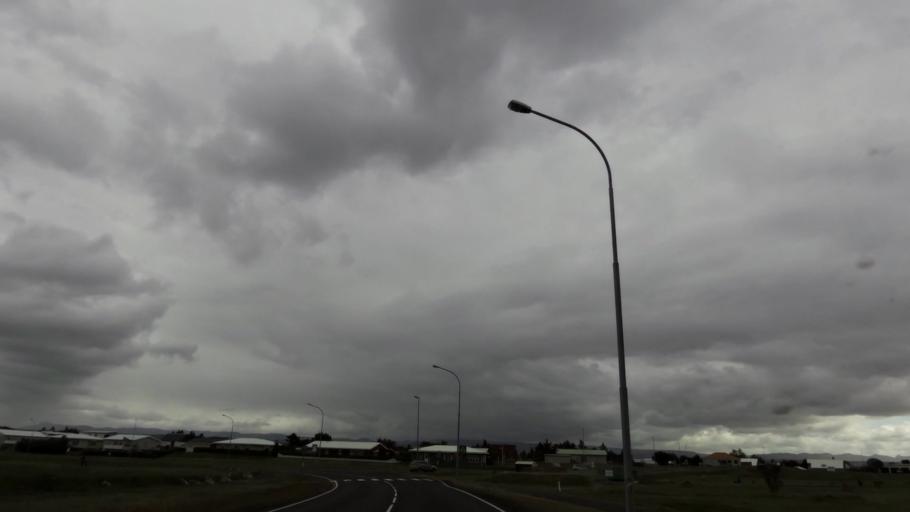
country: IS
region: Capital Region
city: Alftanes
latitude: 64.1004
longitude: -22.0262
